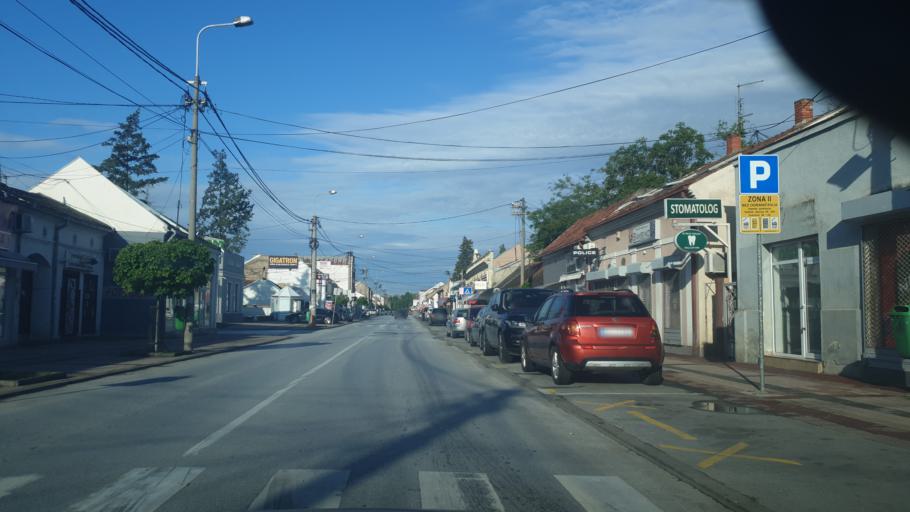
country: RS
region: Central Serbia
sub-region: Belgrade
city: Obrenovac
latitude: 44.6529
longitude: 20.2005
